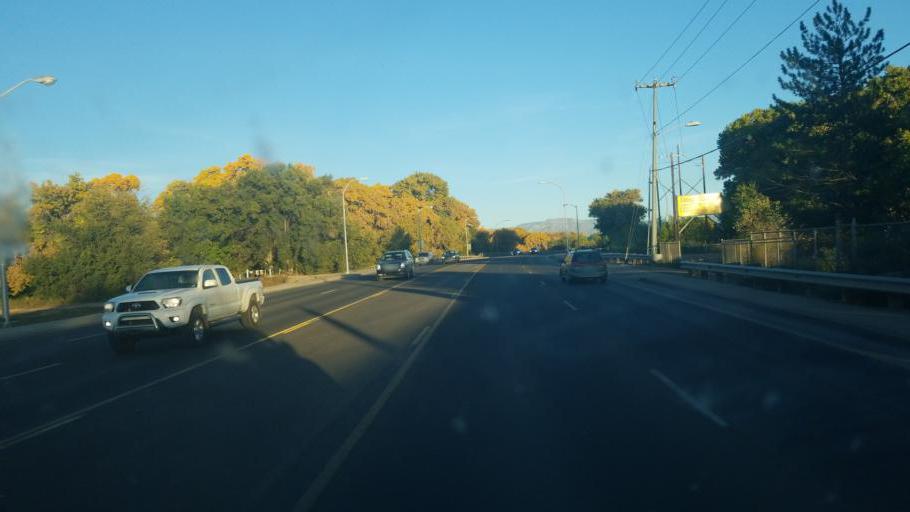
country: US
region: New Mexico
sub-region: Valencia County
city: Los Lunas
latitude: 34.8051
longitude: -106.7214
